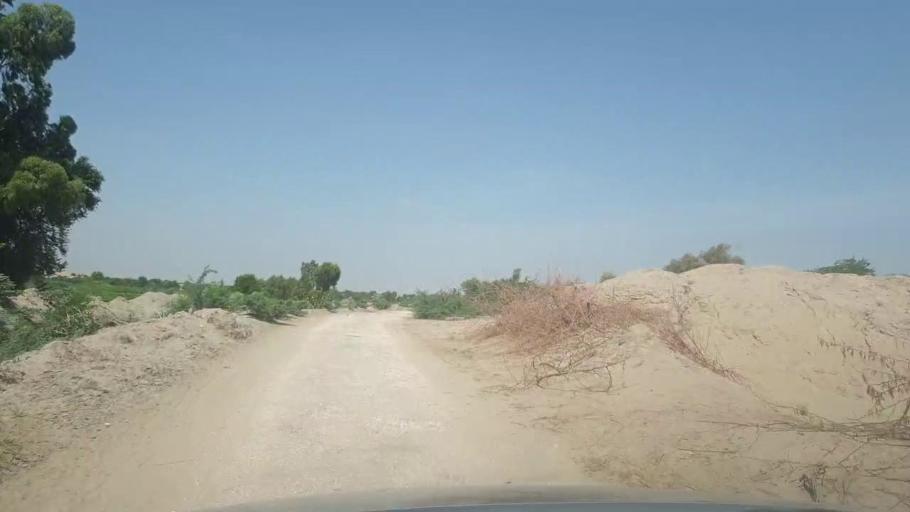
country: PK
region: Sindh
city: Khairpur
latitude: 27.4002
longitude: 69.0410
